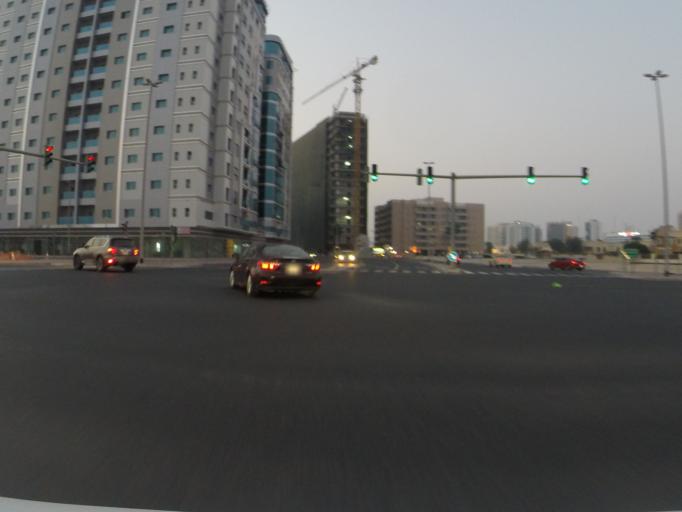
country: AE
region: Dubai
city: Dubai
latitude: 25.1057
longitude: 55.1993
